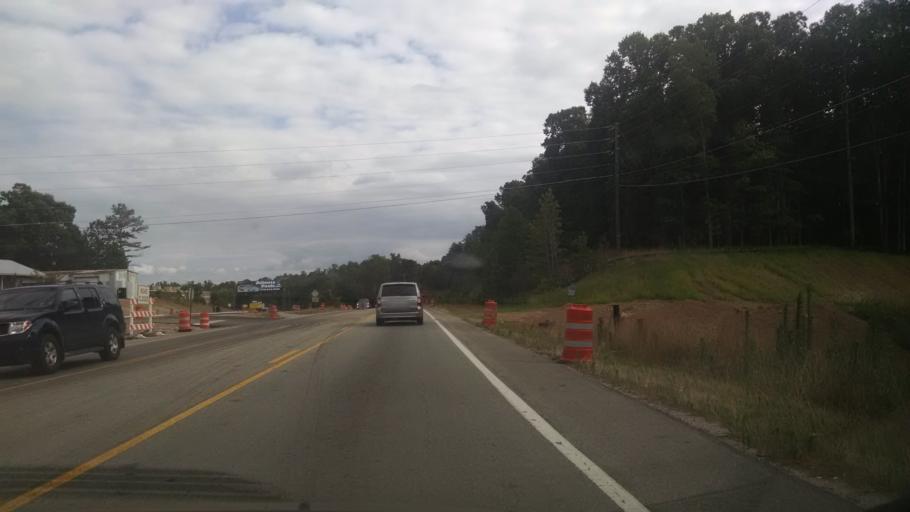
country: US
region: Georgia
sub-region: Forsyth County
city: Cumming
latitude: 34.1445
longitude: -84.1050
